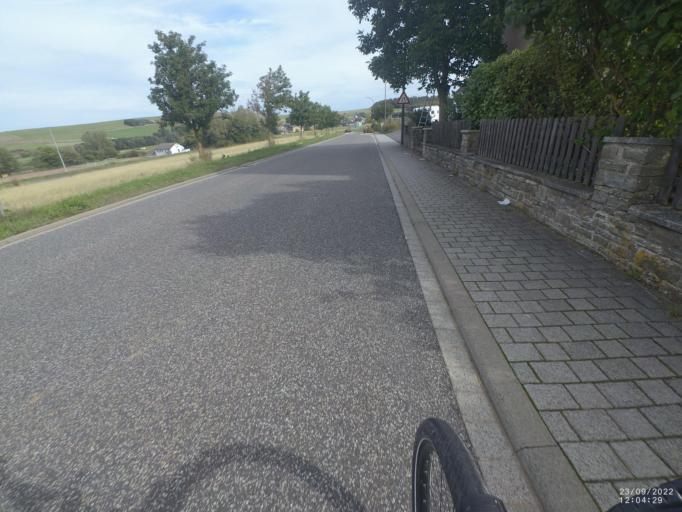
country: DE
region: Rheinland-Pfalz
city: Kirchweiler
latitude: 50.2323
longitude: 6.7491
